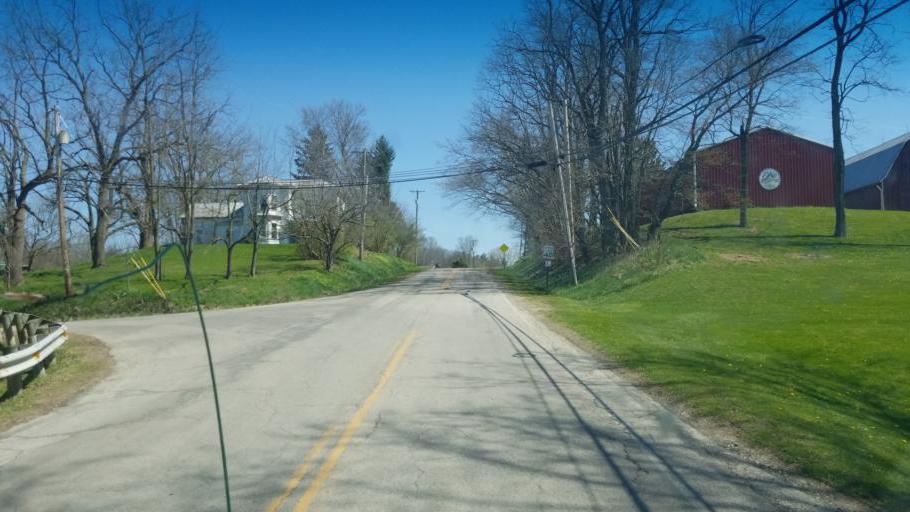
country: US
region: Ohio
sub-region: Richland County
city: Lincoln Heights
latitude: 40.8100
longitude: -82.4345
